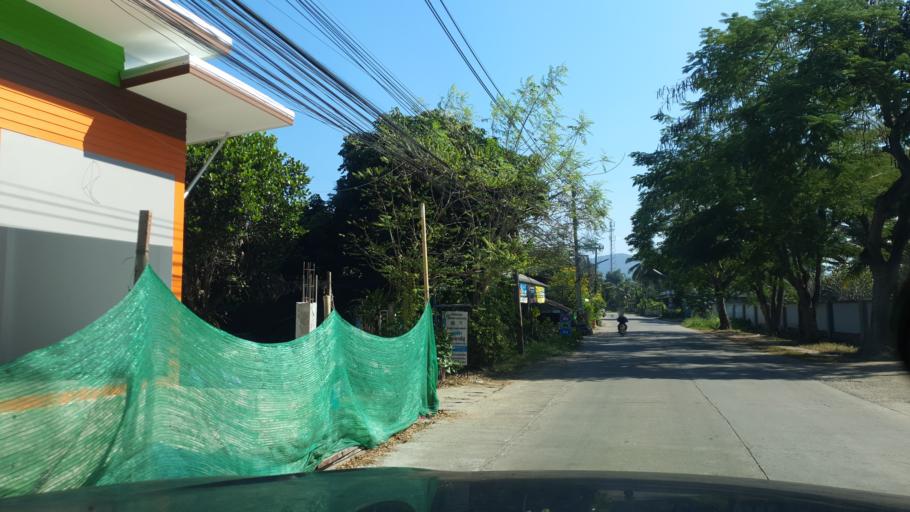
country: TH
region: Chiang Mai
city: San Sai
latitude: 18.8739
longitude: 99.1455
